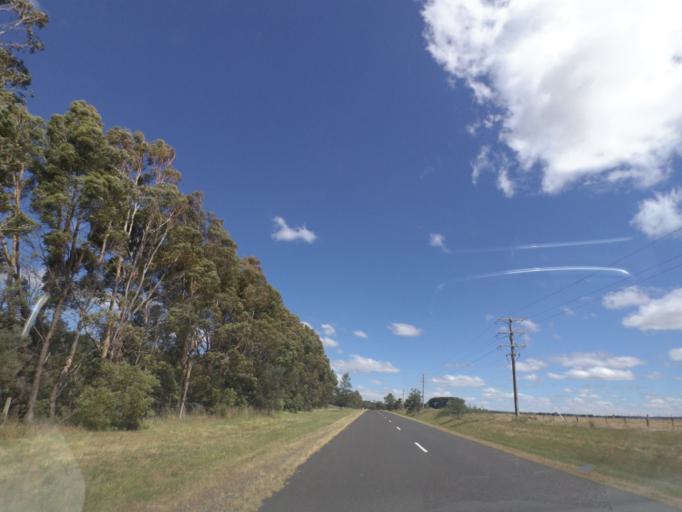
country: AU
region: Victoria
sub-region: Hume
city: Sunbury
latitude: -37.3143
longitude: 144.5193
